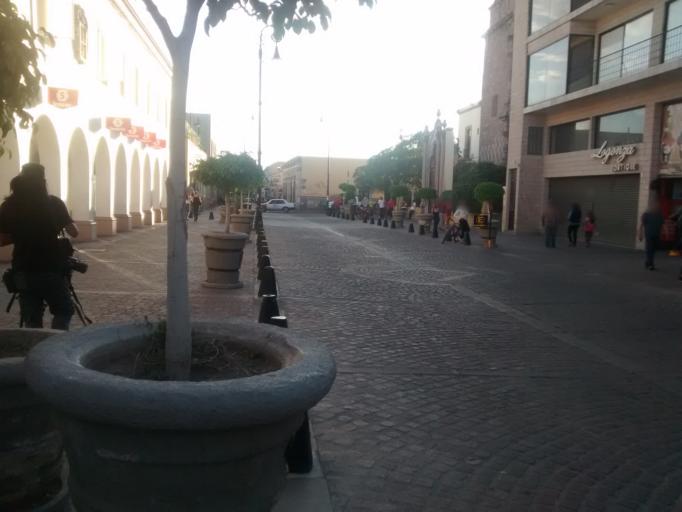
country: MX
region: Aguascalientes
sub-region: Aguascalientes
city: Aguascalientes
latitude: 21.8803
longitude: -102.2992
